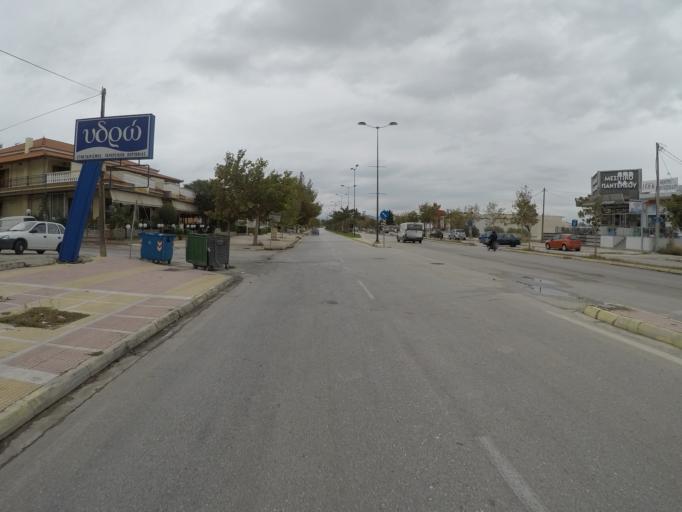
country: GR
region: Peloponnese
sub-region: Nomos Korinthias
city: Loutraki
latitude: 37.9618
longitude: 22.9789
